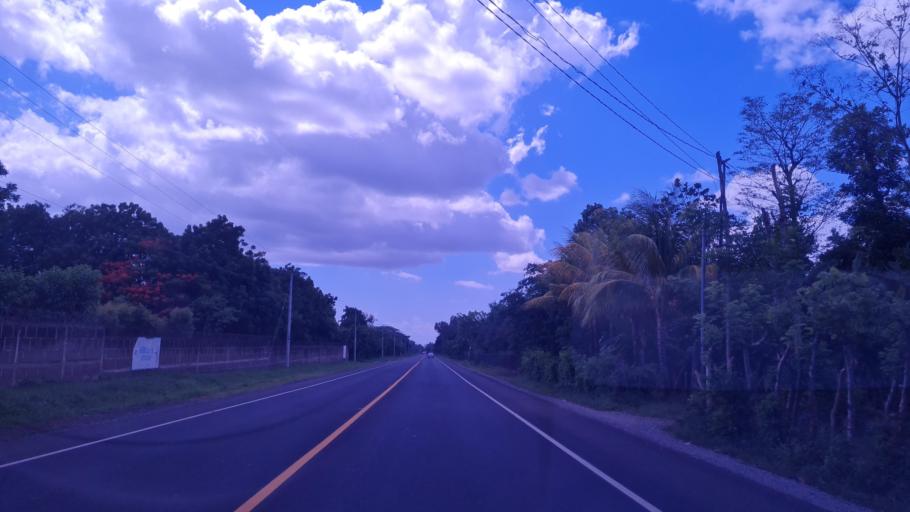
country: NI
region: Masaya
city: Nindiri
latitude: 12.0265
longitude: -86.1220
